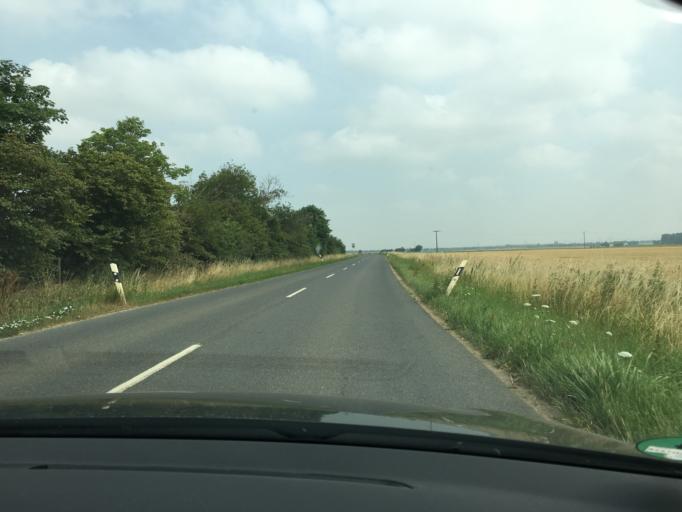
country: DE
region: North Rhine-Westphalia
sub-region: Regierungsbezirk Koln
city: Merzenich
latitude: 50.8210
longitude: 6.5862
